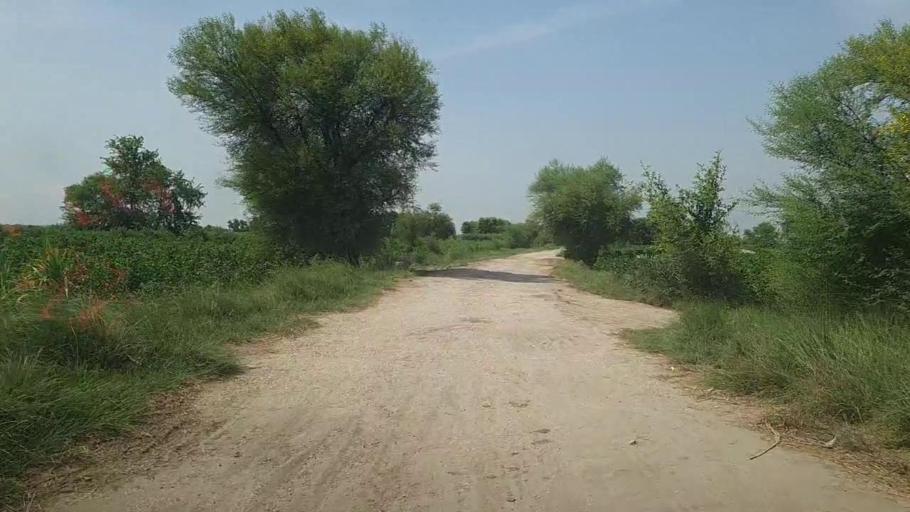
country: PK
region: Sindh
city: Ubauro
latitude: 28.1732
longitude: 69.8154
